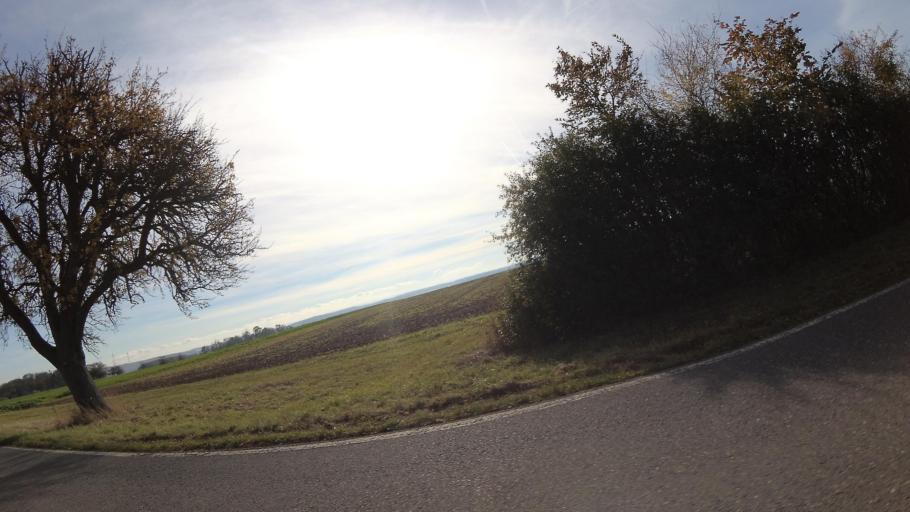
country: DE
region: Baden-Wuerttemberg
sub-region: Regierungsbezirk Stuttgart
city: Mockmuhl
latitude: 49.3208
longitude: 9.3313
